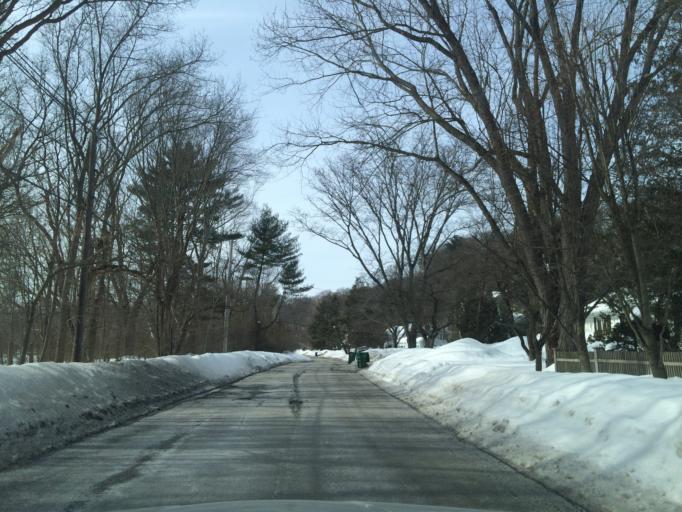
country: US
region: Massachusetts
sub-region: Middlesex County
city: Newton
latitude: 42.3217
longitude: -71.2358
